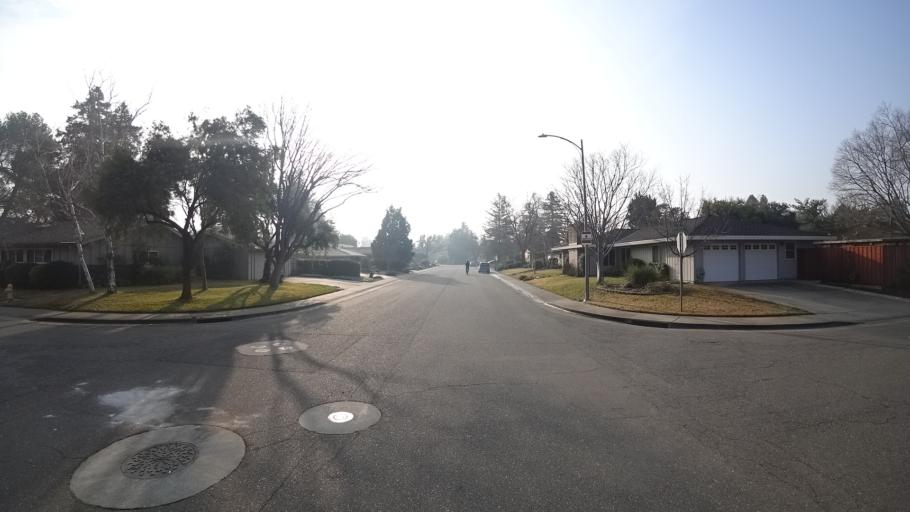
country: US
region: California
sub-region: Yolo County
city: Davis
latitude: 38.5647
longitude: -121.7540
